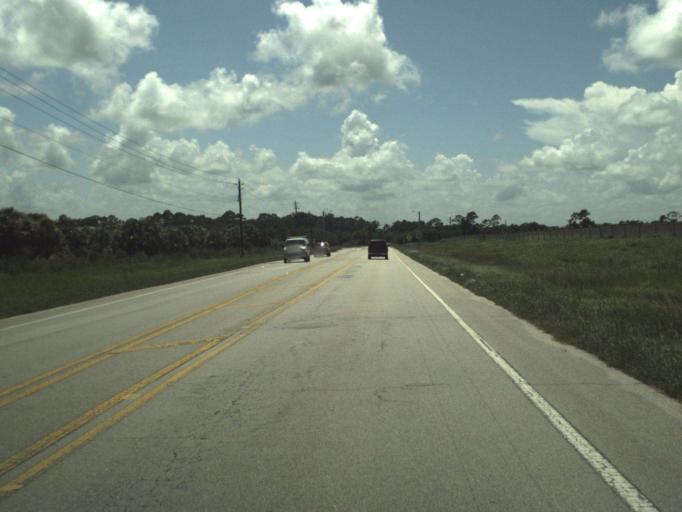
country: US
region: Florida
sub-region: Indian River County
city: Sebastian
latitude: 27.7488
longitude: -80.5045
